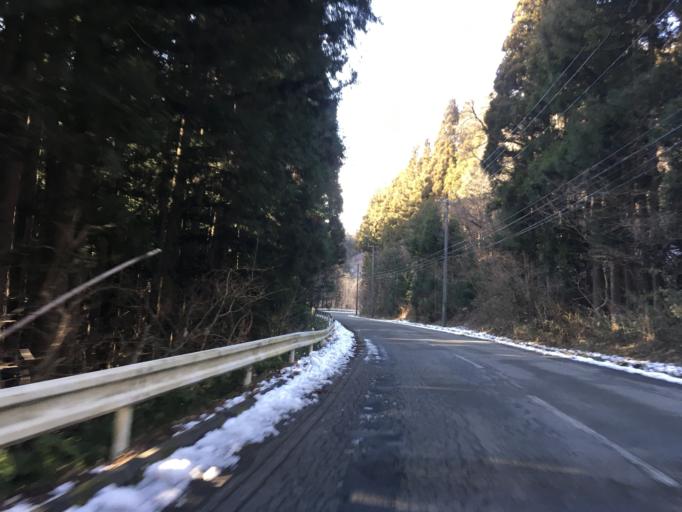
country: JP
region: Miyagi
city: Furukawa
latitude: 38.8039
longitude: 140.8301
